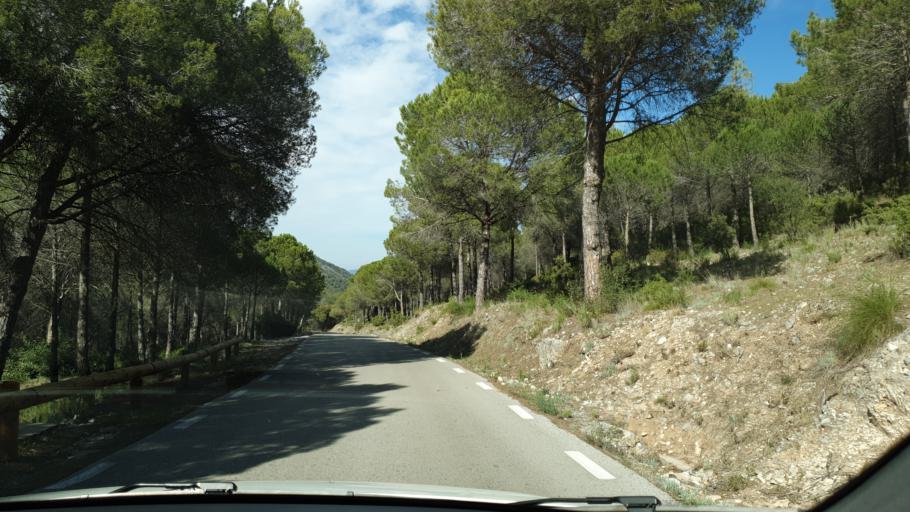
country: ES
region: Andalusia
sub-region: Provincia de Malaga
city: Ojen
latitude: 36.5913
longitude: -4.8575
